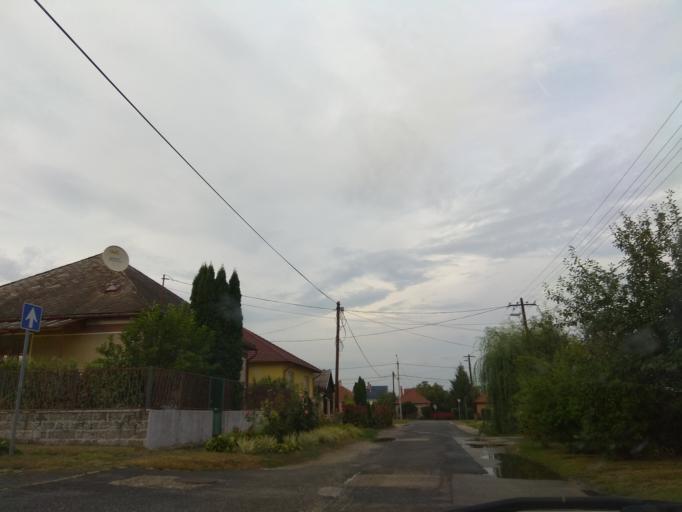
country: HU
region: Borsod-Abauj-Zemplen
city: Miskolc
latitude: 48.0744
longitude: 20.8249
